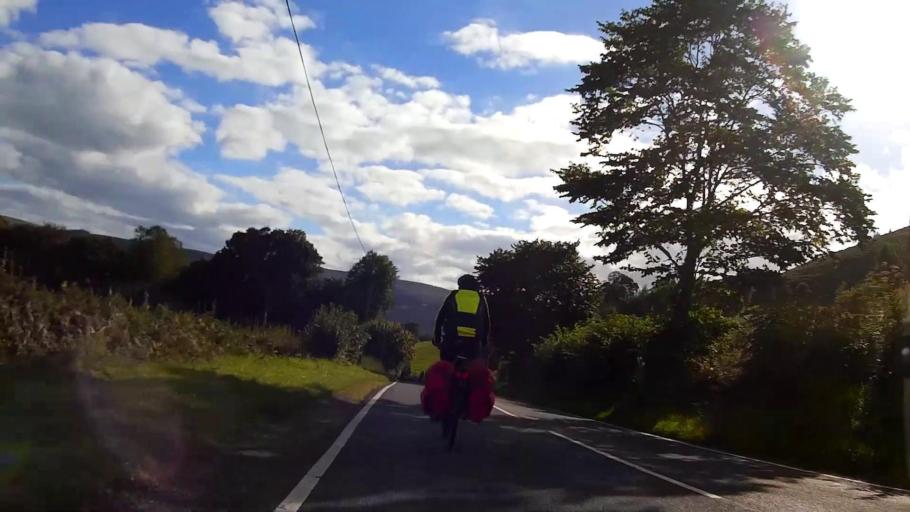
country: GB
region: Wales
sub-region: Denbighshire
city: Llangollen
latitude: 53.0007
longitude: -3.1926
